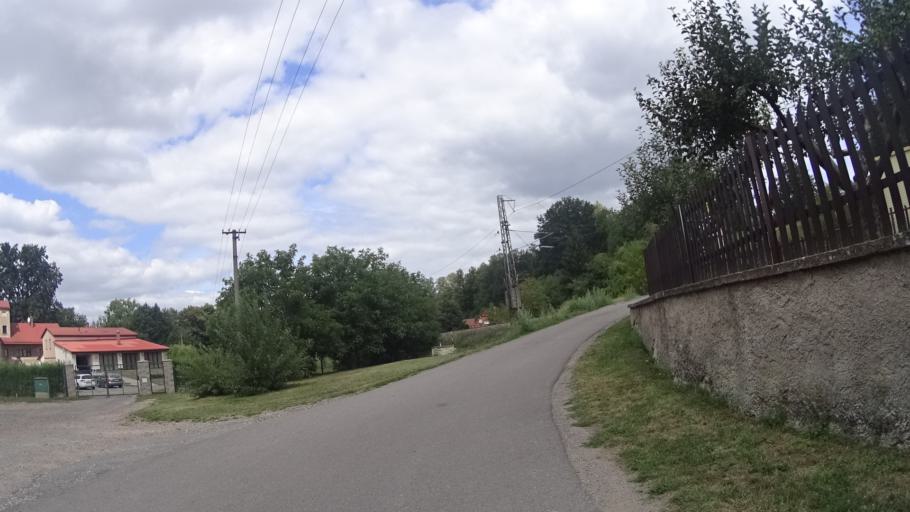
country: CZ
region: Pardubicky
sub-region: Okres Usti nad Orlici
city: Usti nad Orlici
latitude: 49.9864
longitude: 16.4023
